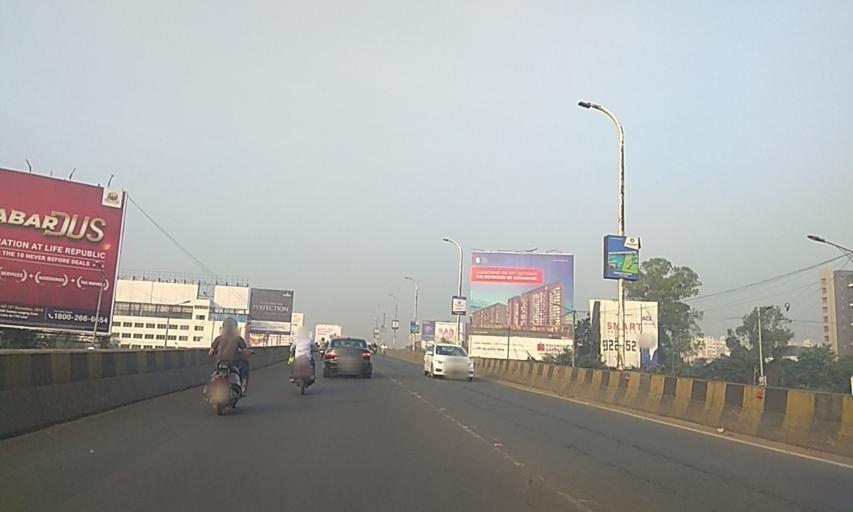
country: IN
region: Maharashtra
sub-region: Pune Division
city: Pimpri
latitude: 18.5923
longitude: 73.7597
